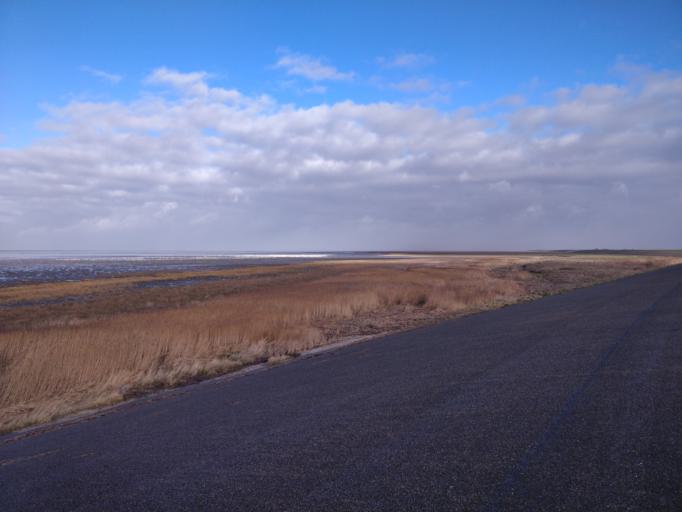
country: NL
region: Friesland
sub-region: Gemeente Het Bildt
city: Sint Jacobiparochie
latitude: 53.3097
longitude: 5.6194
